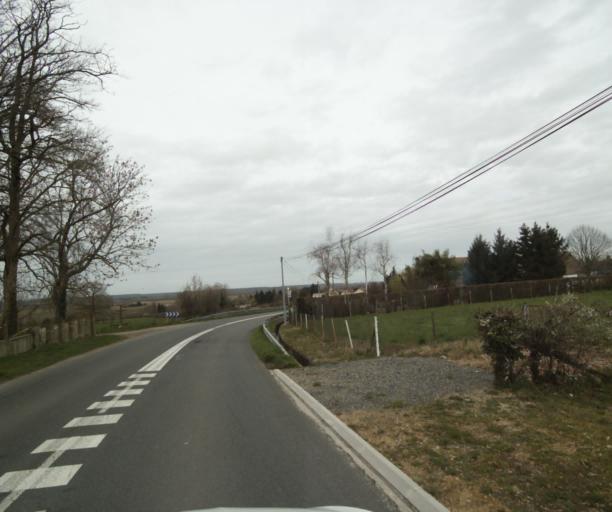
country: FR
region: Auvergne
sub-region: Departement de l'Allier
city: Toulon-sur-Allier
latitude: 46.5076
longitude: 3.3679
